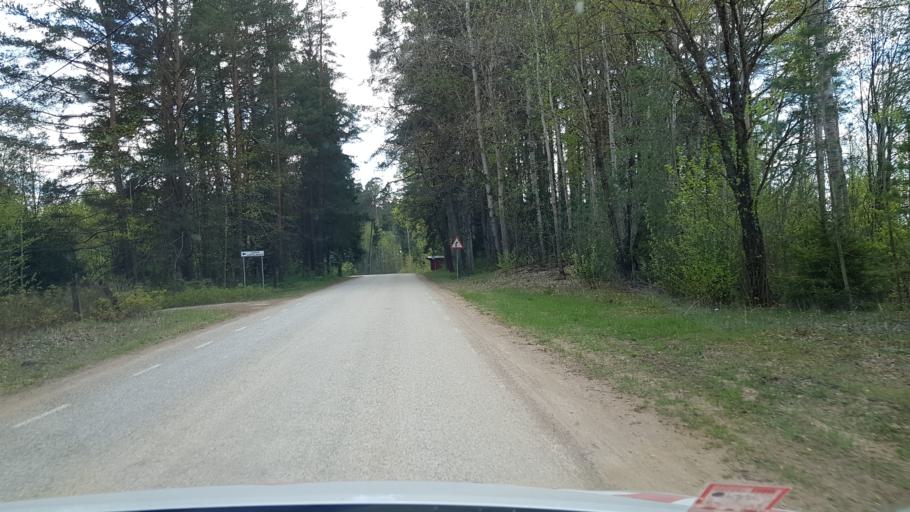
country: EE
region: Tartu
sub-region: UElenurme vald
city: Ulenurme
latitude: 58.3450
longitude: 26.8403
